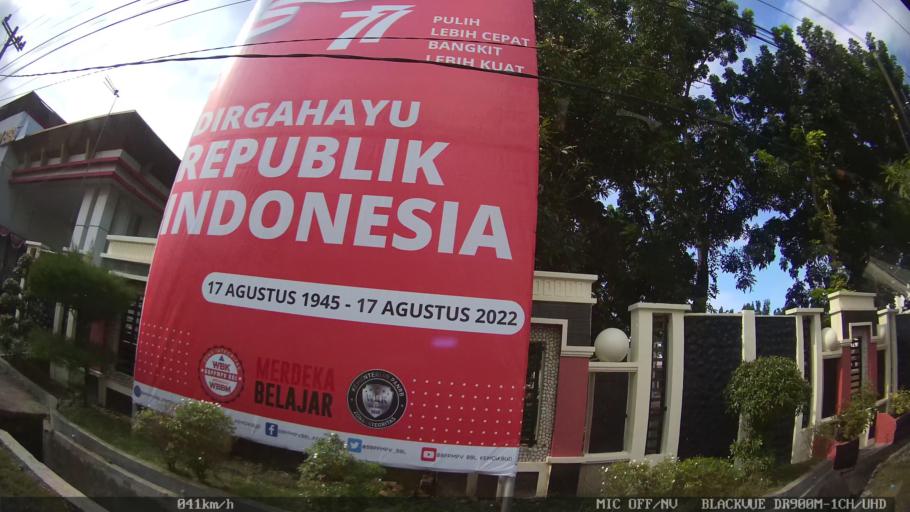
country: ID
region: North Sumatra
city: Medan
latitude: 3.6152
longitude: 98.6568
